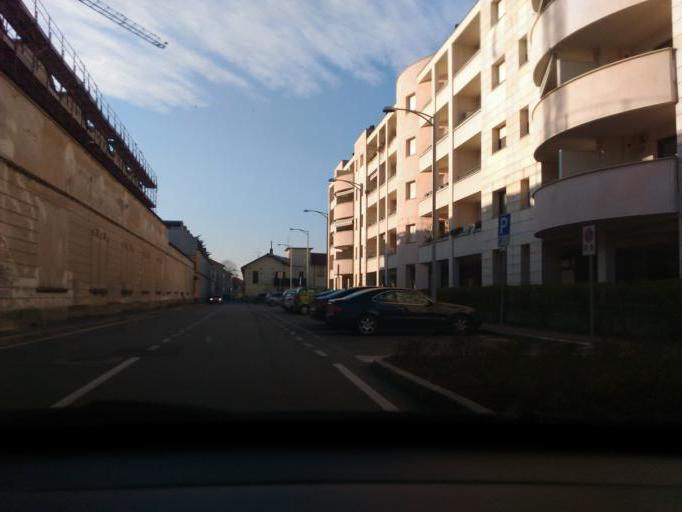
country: IT
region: Lombardy
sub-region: Provincia di Varese
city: Busto Arsizio
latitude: 45.6093
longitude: 8.8472
